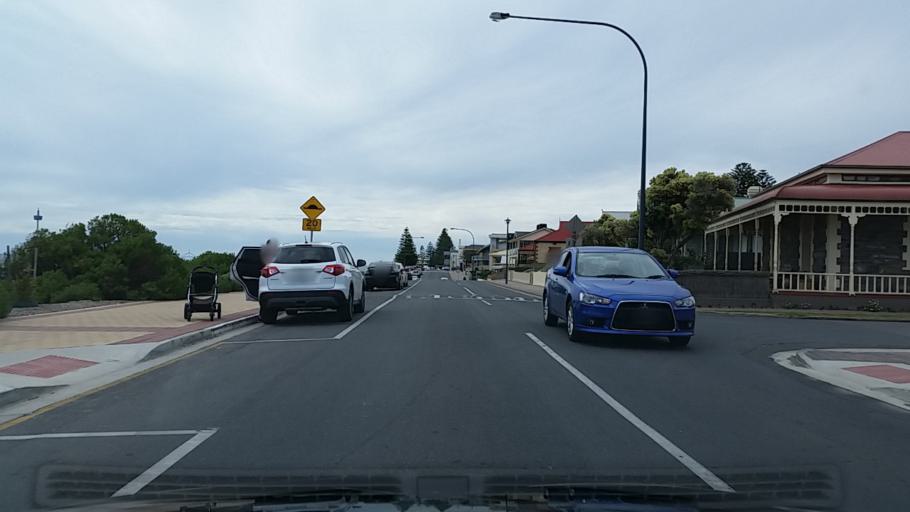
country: AU
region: South Australia
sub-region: Adelaide
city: Brighton
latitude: -35.0207
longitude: 138.5158
